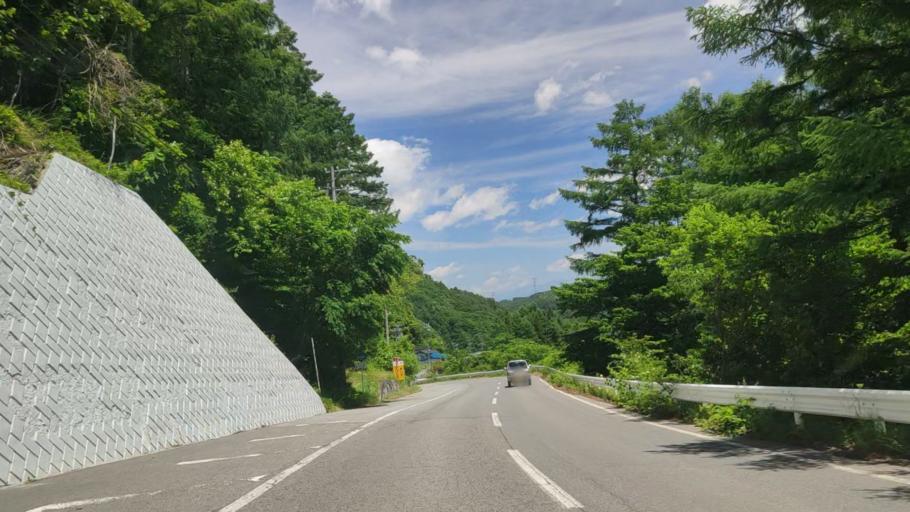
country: JP
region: Nagano
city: Kamimaruko
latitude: 36.1701
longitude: 138.2405
